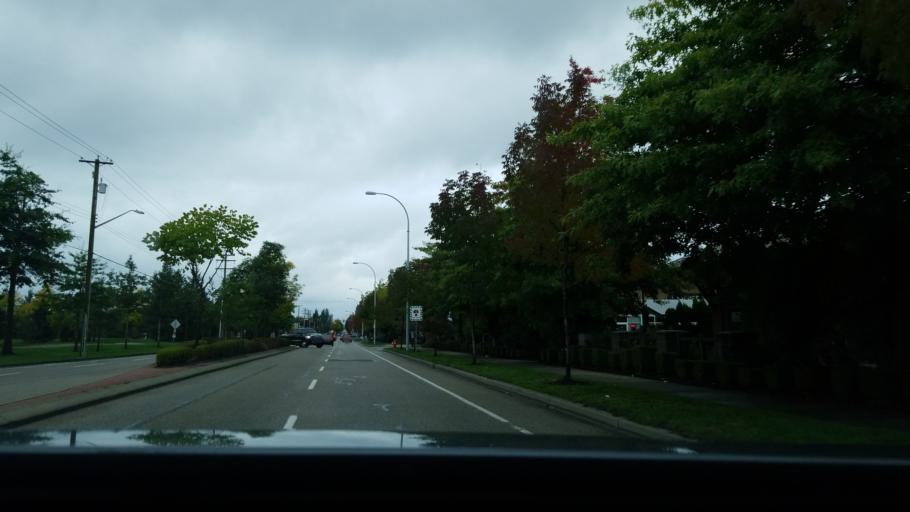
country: CA
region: British Columbia
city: Langley
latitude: 49.1189
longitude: -122.7315
